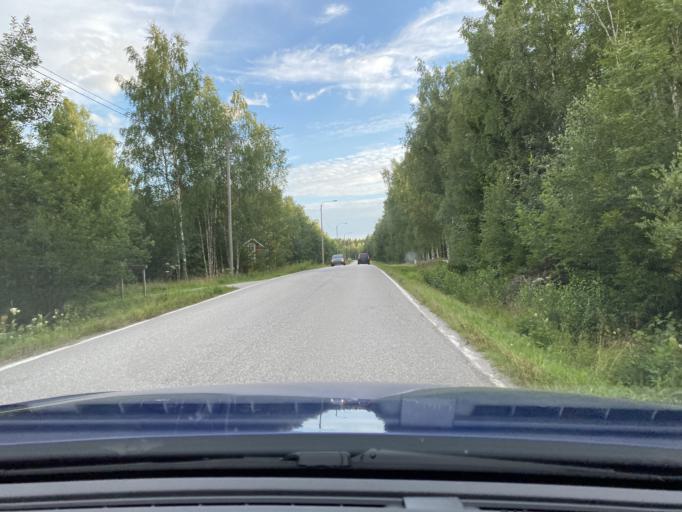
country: FI
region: Ostrobothnia
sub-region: Vaasa
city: Korsnaes
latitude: 62.9566
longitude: 21.1824
